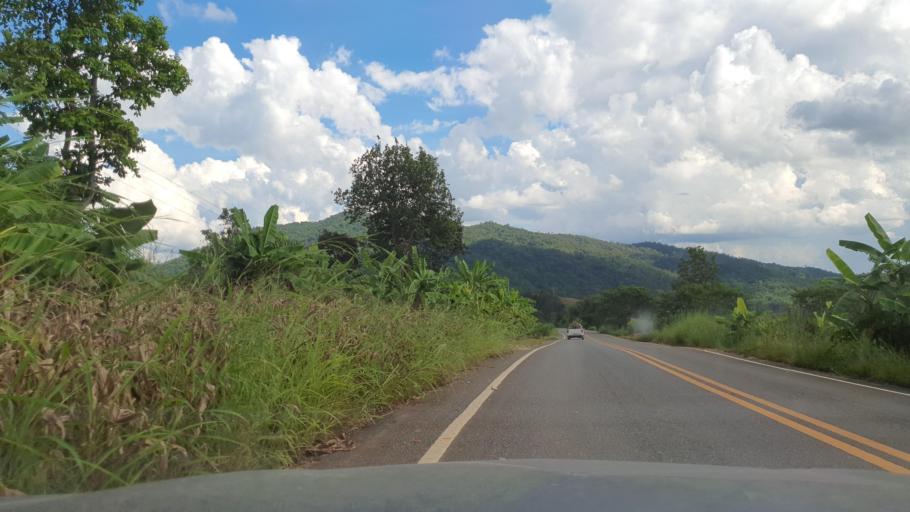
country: TH
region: Chiang Rai
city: Wiang Pa Pao
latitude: 19.3121
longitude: 99.4064
